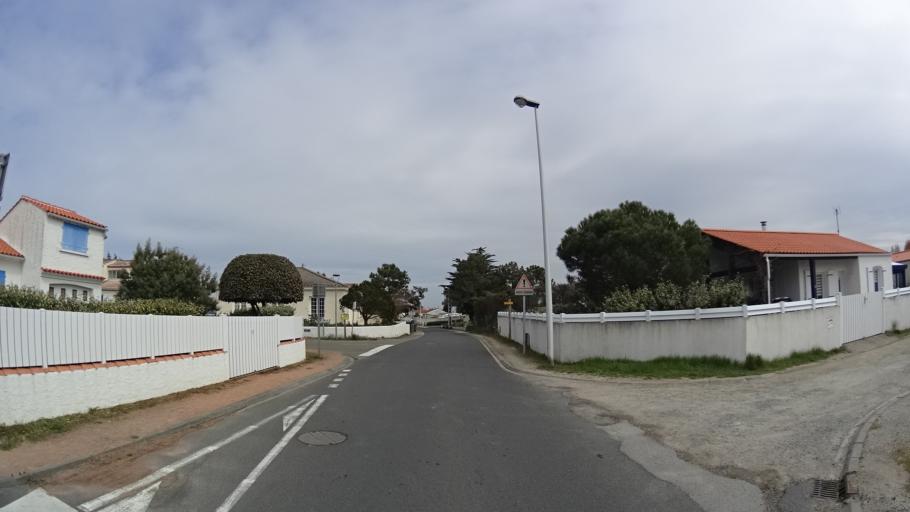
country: FR
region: Pays de la Loire
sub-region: Departement de la Vendee
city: La Barre-de-Monts
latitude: 46.8863
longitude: -2.1228
